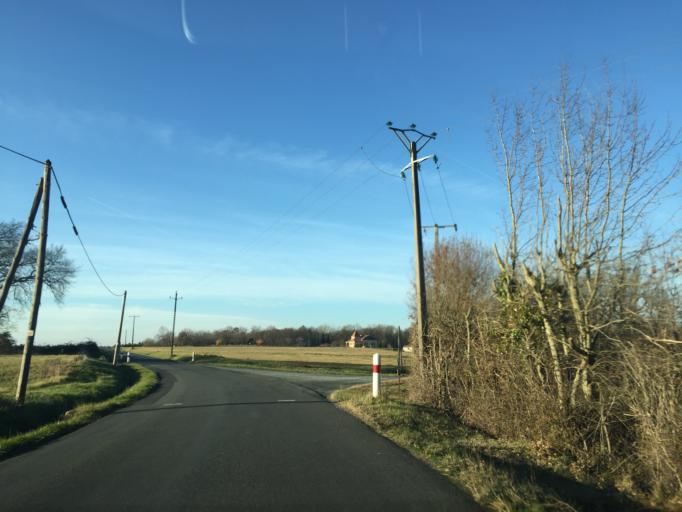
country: FR
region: Aquitaine
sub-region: Departement de la Dordogne
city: Riberac
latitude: 45.2114
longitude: 0.2999
